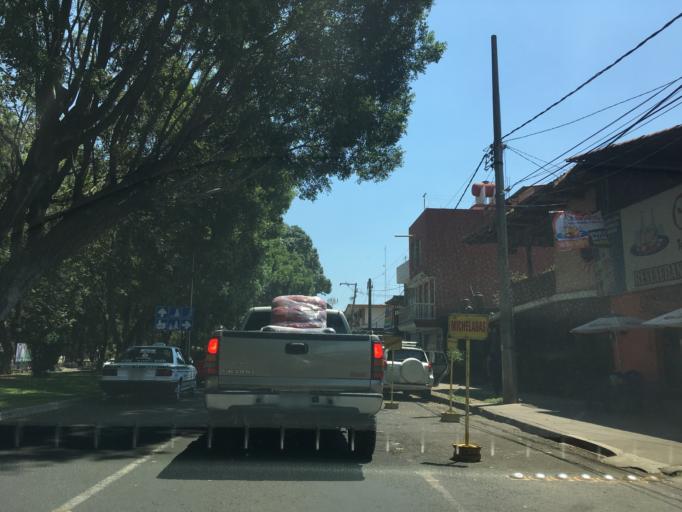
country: MX
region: Michoacan
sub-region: Uruapan
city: Uruapan
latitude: 19.4170
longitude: -102.0511
